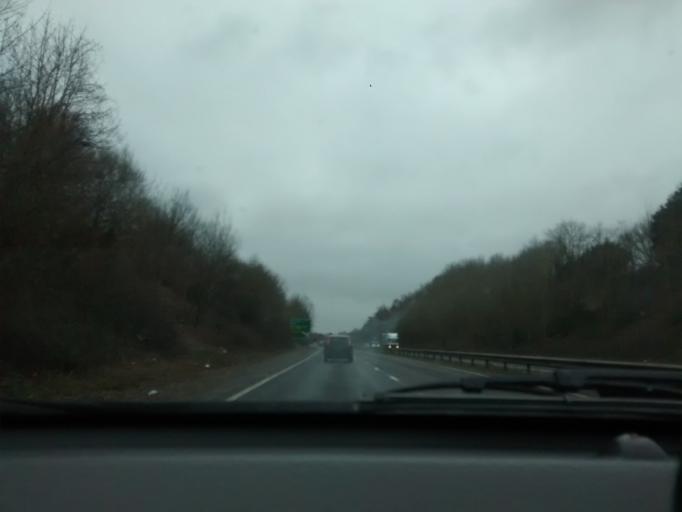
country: GB
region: England
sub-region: Suffolk
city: Needham Market
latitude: 52.1566
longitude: 1.0650
